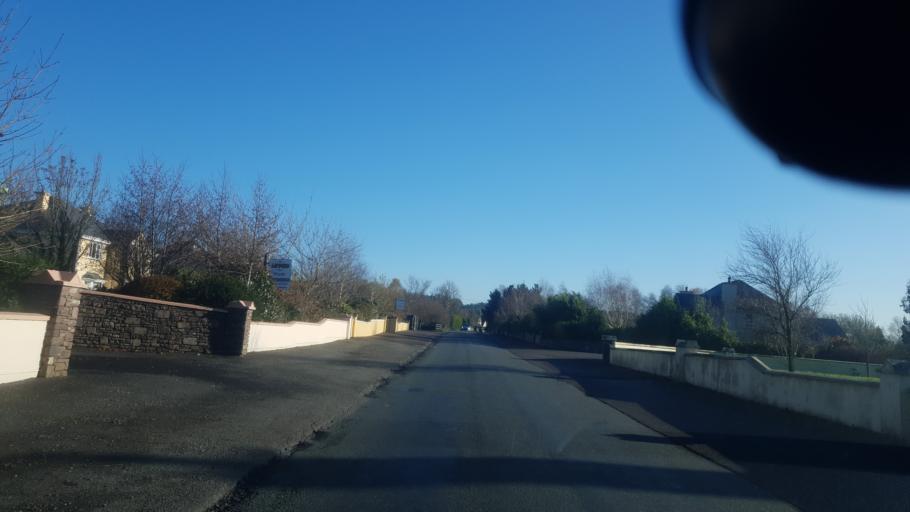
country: IE
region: Munster
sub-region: Ciarrai
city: Cill Airne
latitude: 52.1130
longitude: -9.5144
